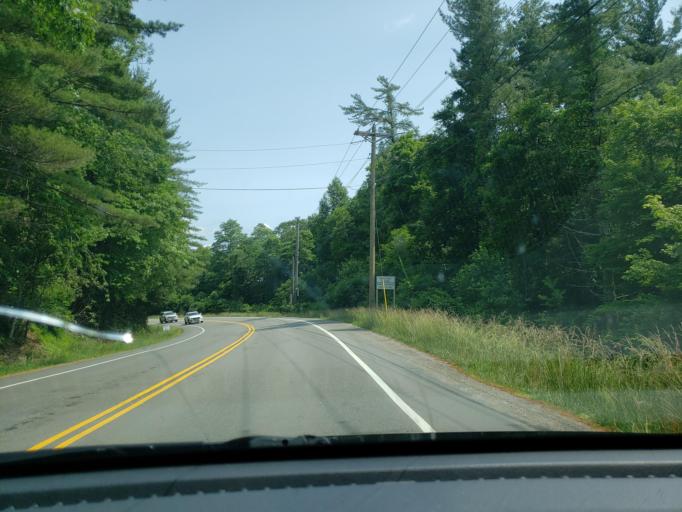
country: US
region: North Carolina
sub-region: Watauga County
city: Blowing Rock
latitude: 36.1376
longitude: -81.6852
